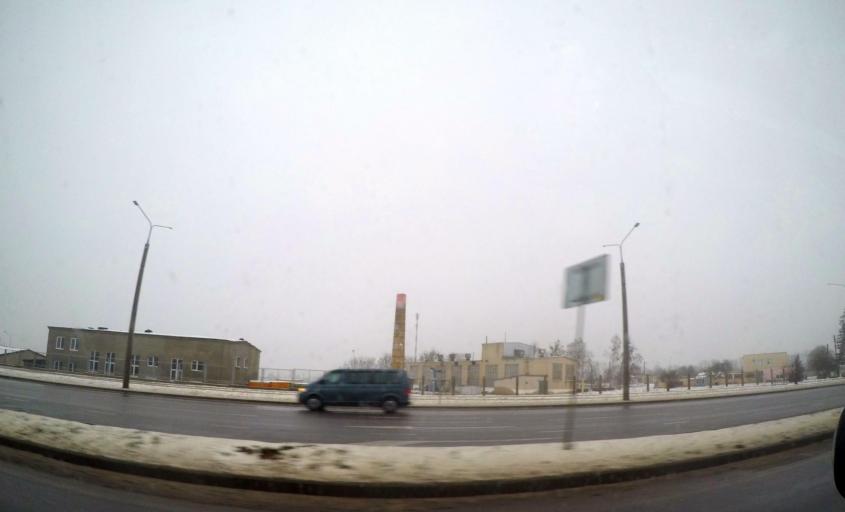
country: BY
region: Grodnenskaya
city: Hrodna
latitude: 53.6395
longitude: 23.8153
